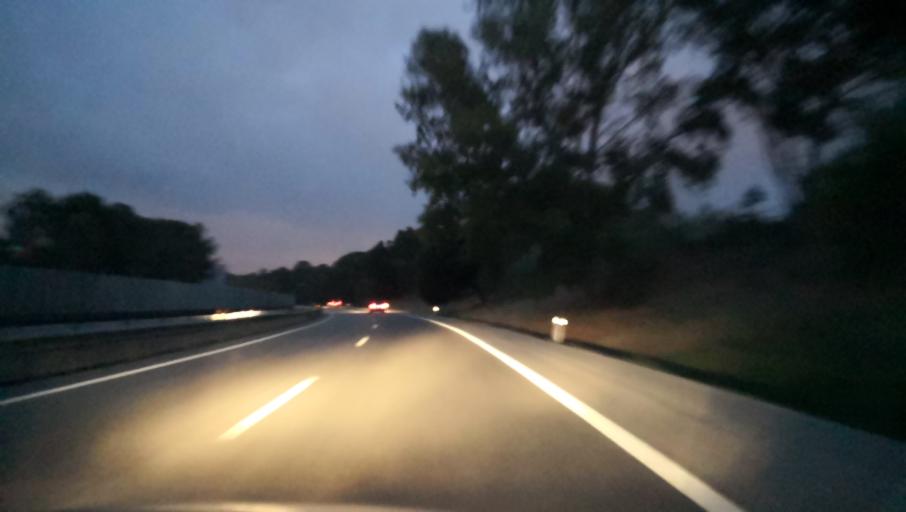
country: PT
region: Setubal
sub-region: Barreiro
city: Santo Antonio da Charneca
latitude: 38.6282
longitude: -9.0378
